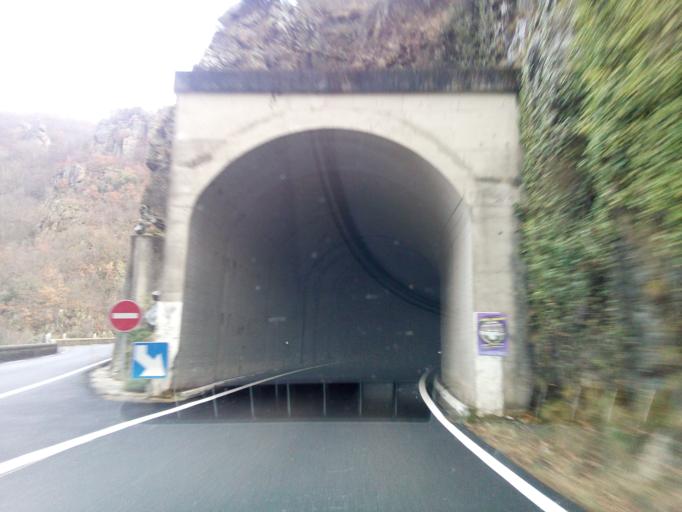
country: FR
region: Rhone-Alpes
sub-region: Departement de l'Ardeche
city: Saint-Sauveur-de-Montagut
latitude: 44.8816
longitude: 4.5300
